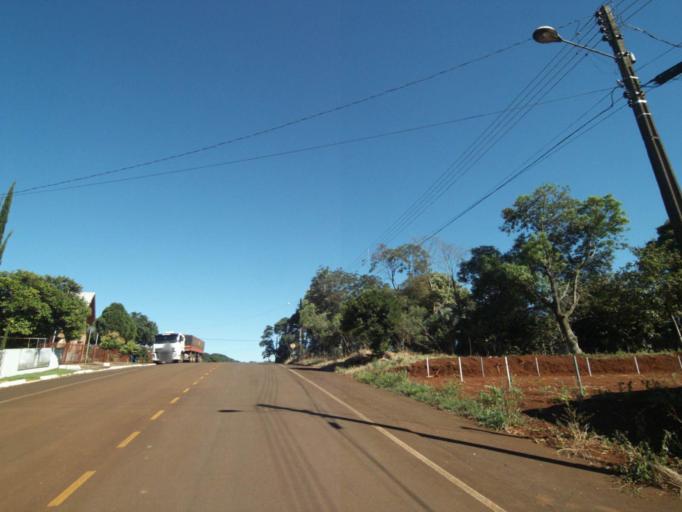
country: BR
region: Parana
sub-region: Pato Branco
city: Pato Branco
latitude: -26.2592
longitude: -52.7757
